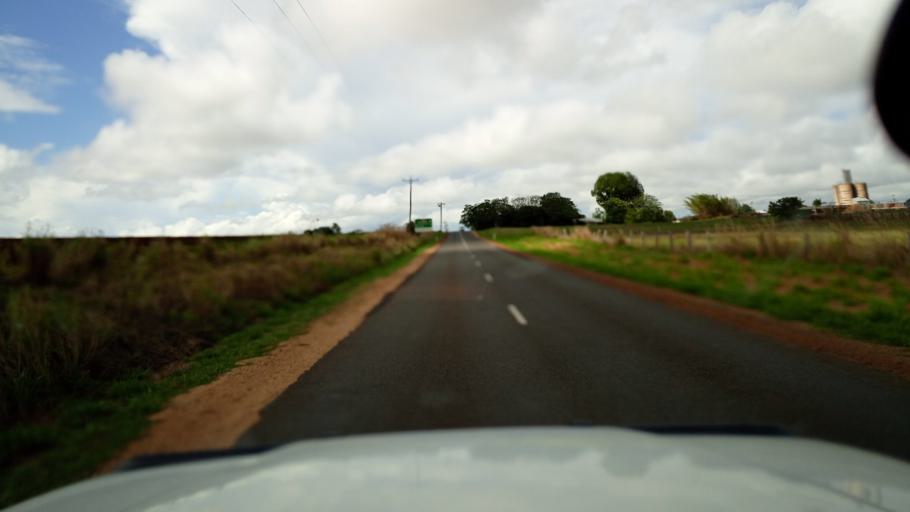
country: AU
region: Queensland
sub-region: Tablelands
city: Tolga
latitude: -17.2201
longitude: 145.5378
